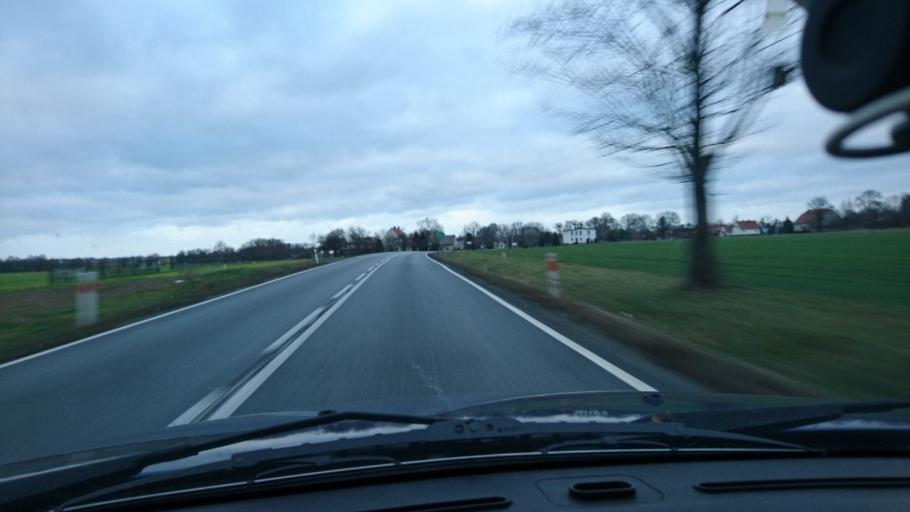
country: PL
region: Opole Voivodeship
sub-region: Powiat kluczborski
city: Byczyna
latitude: 51.0586
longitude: 18.1988
